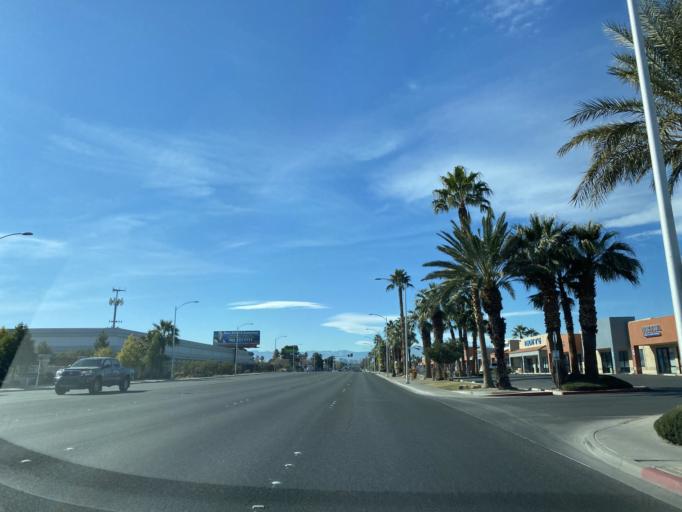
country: US
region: Nevada
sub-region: Clark County
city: Sunrise Manor
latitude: 36.1740
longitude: -115.0659
